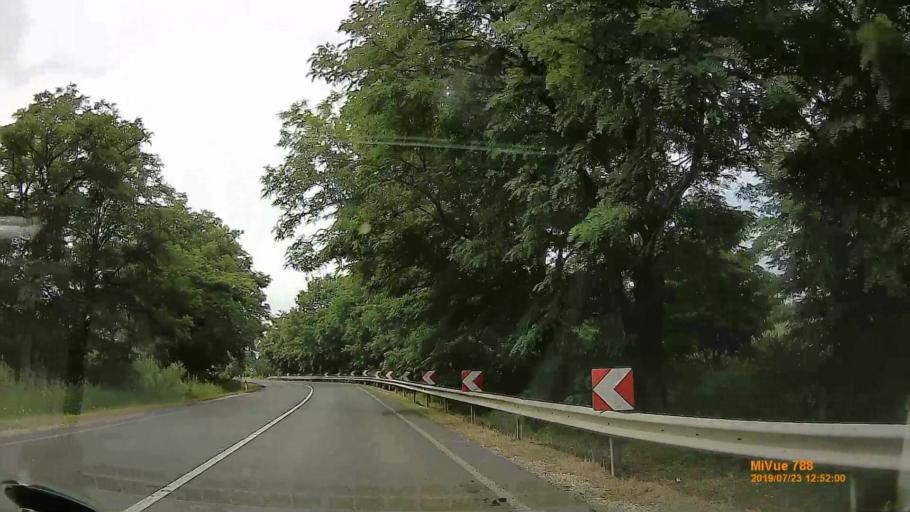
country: HU
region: Szabolcs-Szatmar-Bereg
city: Nagycserkesz
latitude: 47.9613
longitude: 21.5740
